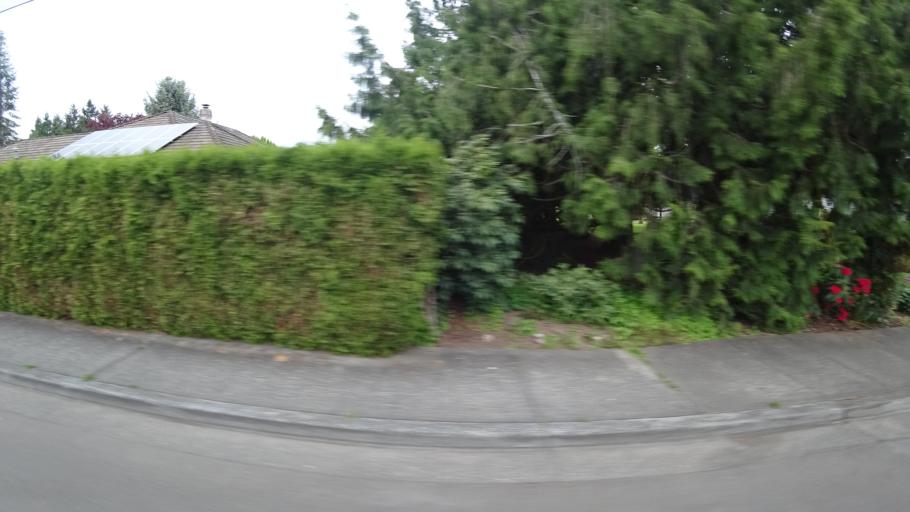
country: US
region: Oregon
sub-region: Washington County
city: Hillsboro
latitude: 45.5443
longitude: -122.9775
